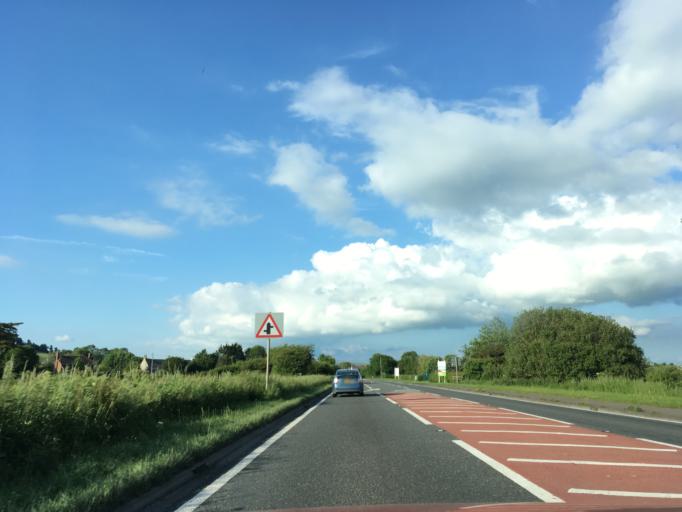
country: GB
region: England
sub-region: Somerset
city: Highbridge
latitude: 51.2451
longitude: -2.9442
